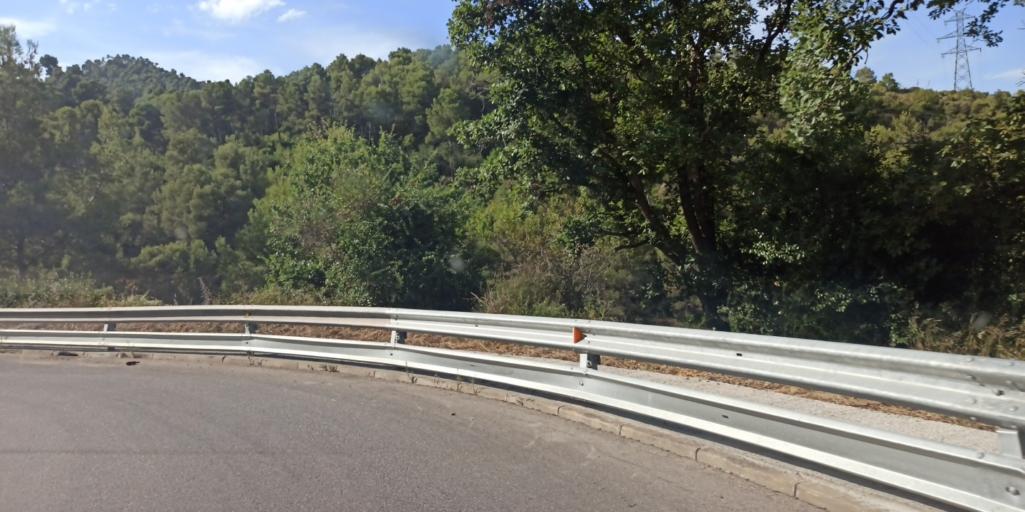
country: ES
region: Catalonia
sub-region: Provincia de Barcelona
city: Santa Coloma de Cervello
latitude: 41.3610
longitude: 2.0069
